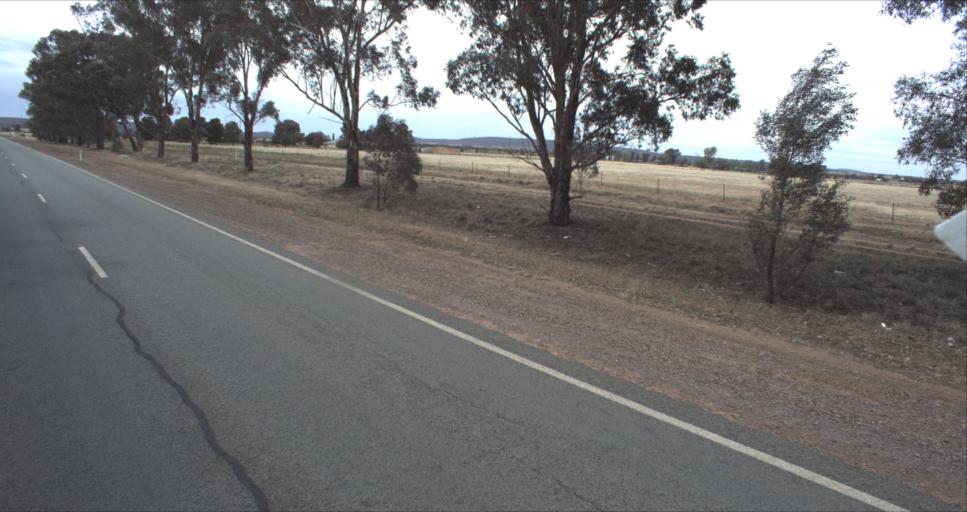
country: AU
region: New South Wales
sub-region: Leeton
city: Leeton
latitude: -34.5139
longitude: 146.4184
